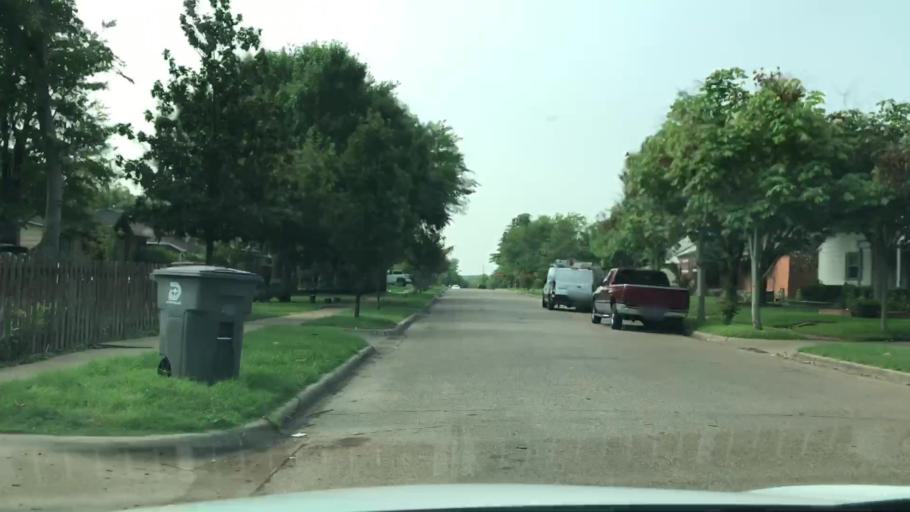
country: US
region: Texas
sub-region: Dallas County
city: Cockrell Hill
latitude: 32.7529
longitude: -96.8689
